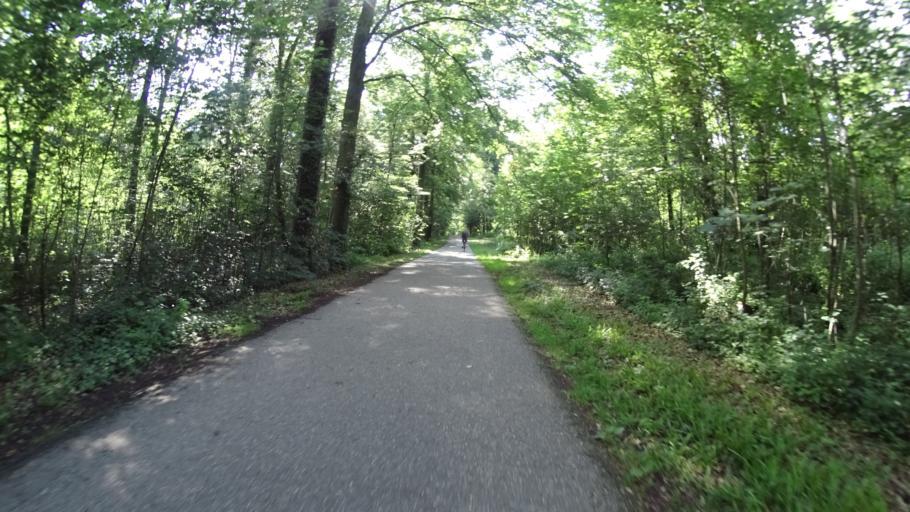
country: DE
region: Baden-Wuerttemberg
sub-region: Karlsruhe Region
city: Karlsruhe
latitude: 48.9862
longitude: 8.4314
